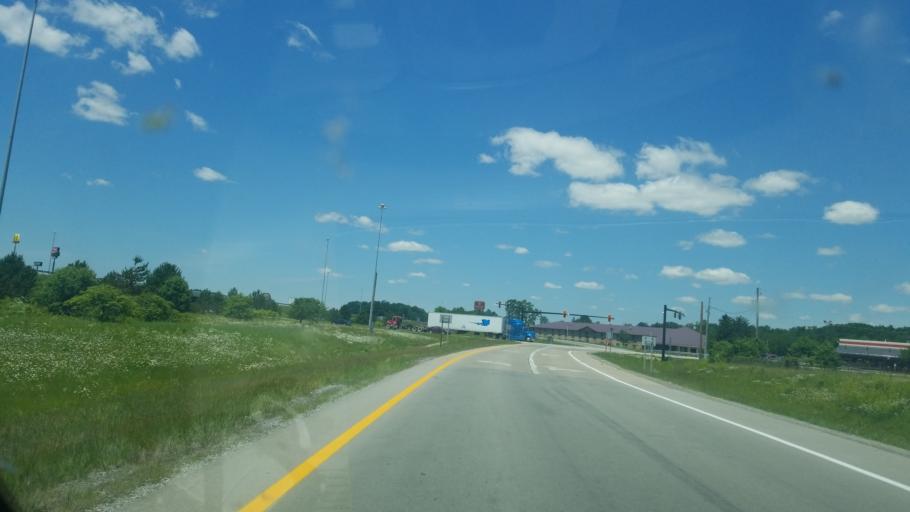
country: US
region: Ohio
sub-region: Wyandot County
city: Upper Sandusky
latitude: 40.8341
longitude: -83.2386
